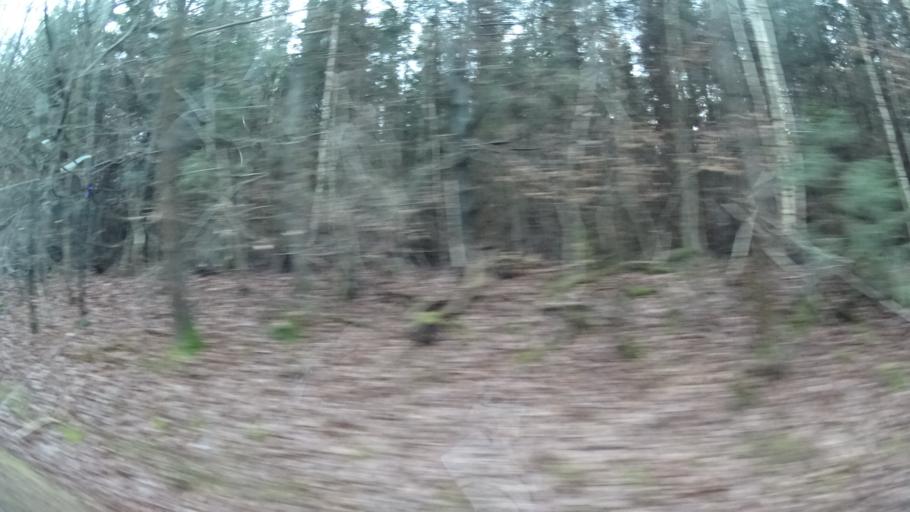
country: DE
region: Hesse
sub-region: Regierungsbezirk Giessen
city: Lauterbach
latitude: 50.6577
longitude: 9.4250
